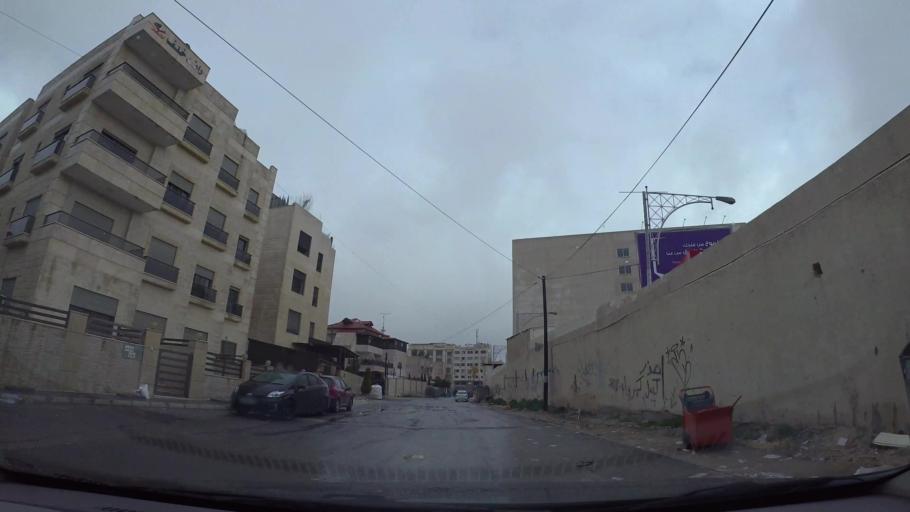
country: JO
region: Amman
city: Wadi as Sir
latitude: 31.9730
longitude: 35.8644
